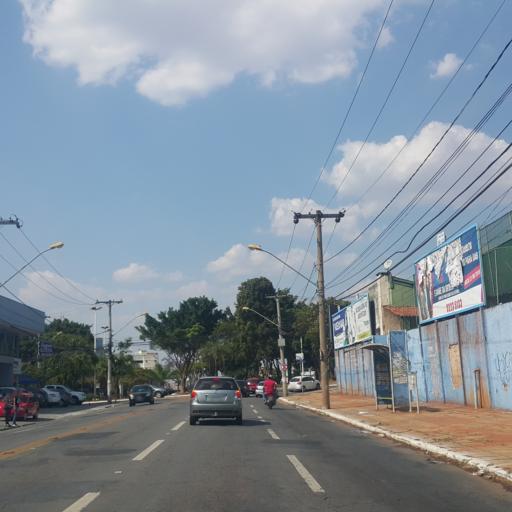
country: BR
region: Goias
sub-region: Goiania
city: Goiania
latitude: -16.6902
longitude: -49.2548
